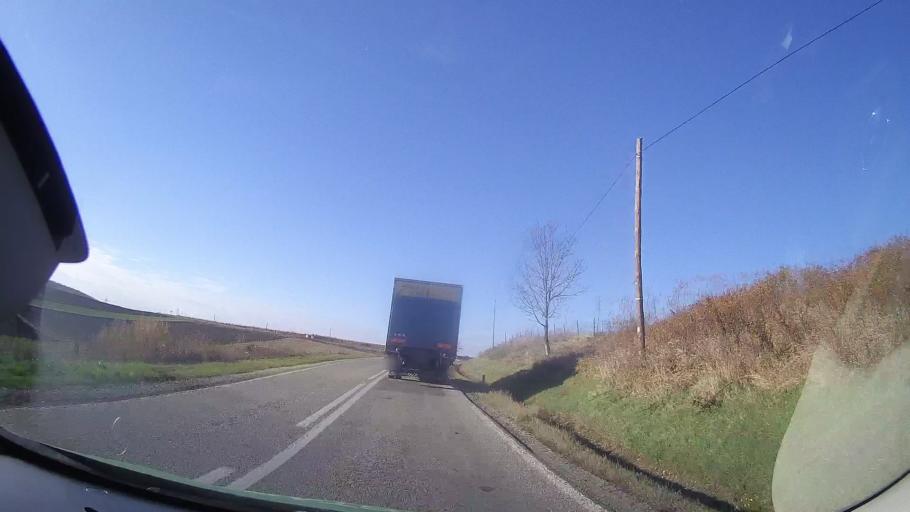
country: RO
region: Cluj
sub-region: Comuna Camarasu
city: Camarasu
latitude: 46.7946
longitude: 24.1084
